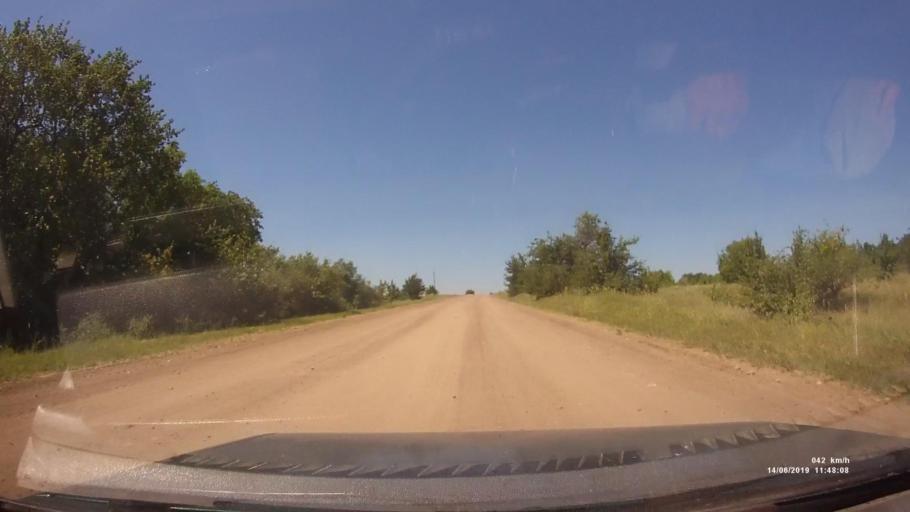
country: RU
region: Rostov
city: Kazanskaya
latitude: 49.8520
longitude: 41.2889
